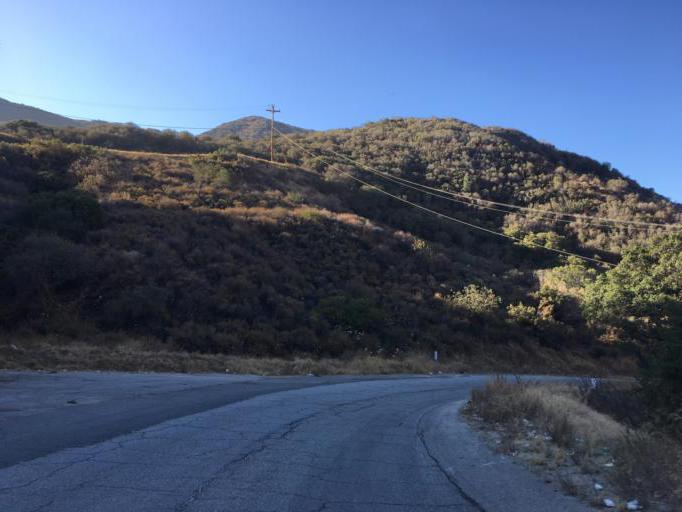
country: US
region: California
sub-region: Los Angeles County
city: San Fernando
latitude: 34.3196
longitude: -118.3386
